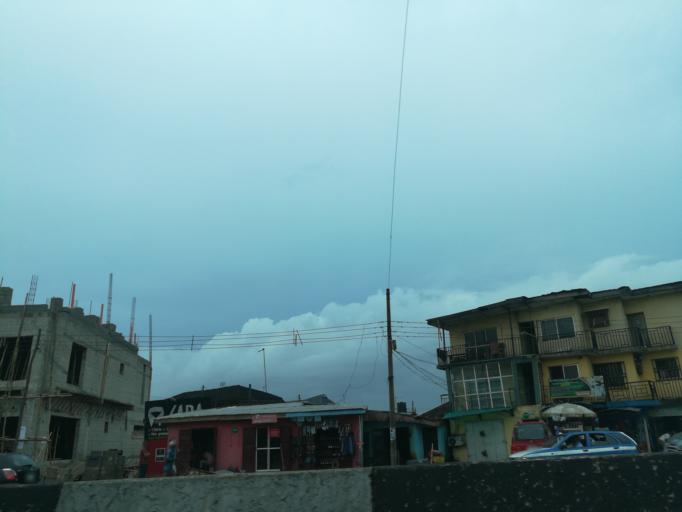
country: NG
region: Rivers
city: Port Harcourt
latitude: 4.8150
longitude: 7.0099
